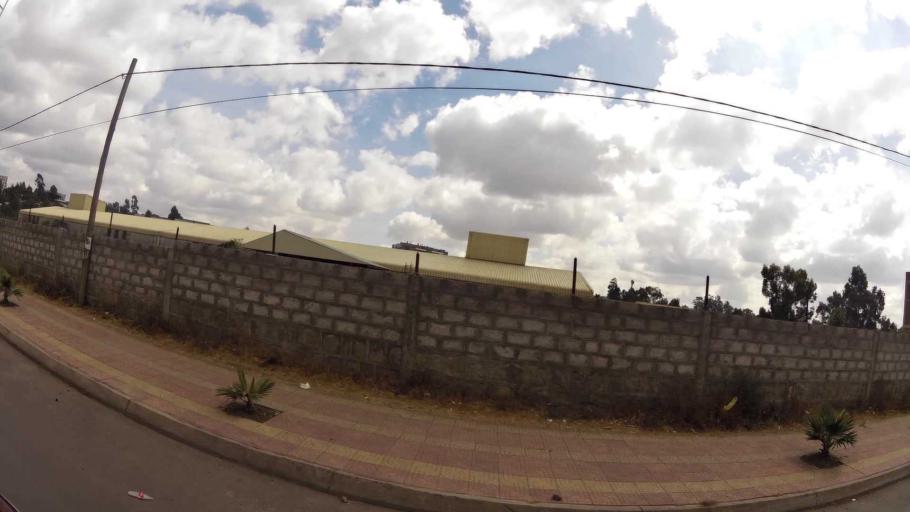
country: ET
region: Adis Abeba
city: Addis Ababa
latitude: 8.9473
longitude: 38.7584
